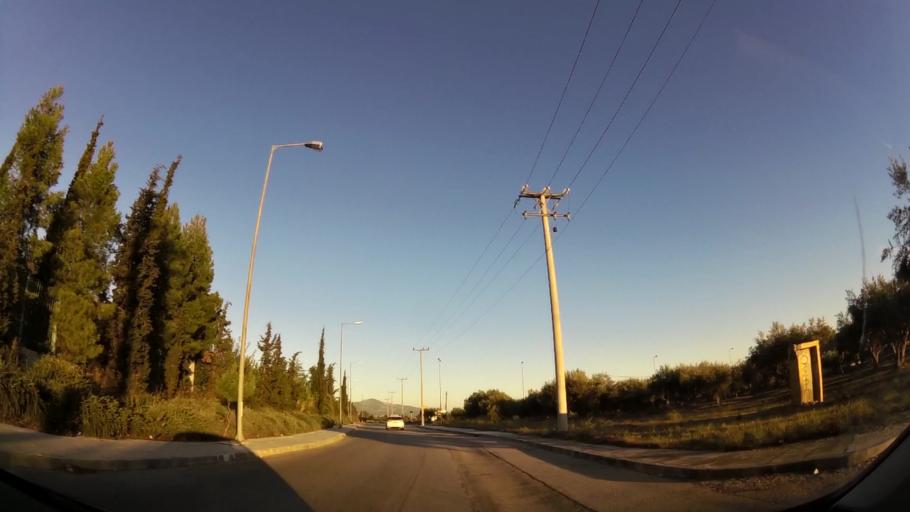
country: GR
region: Attica
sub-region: Nomarchia Dytikis Attikis
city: Ano Liosia
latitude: 38.0806
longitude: 23.6860
